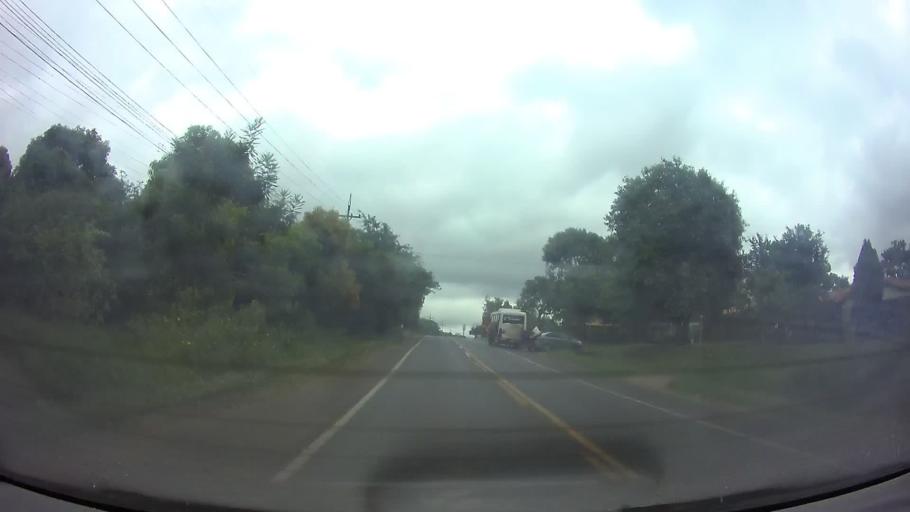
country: PY
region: Central
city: Guarambare
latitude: -25.4998
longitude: -57.4860
